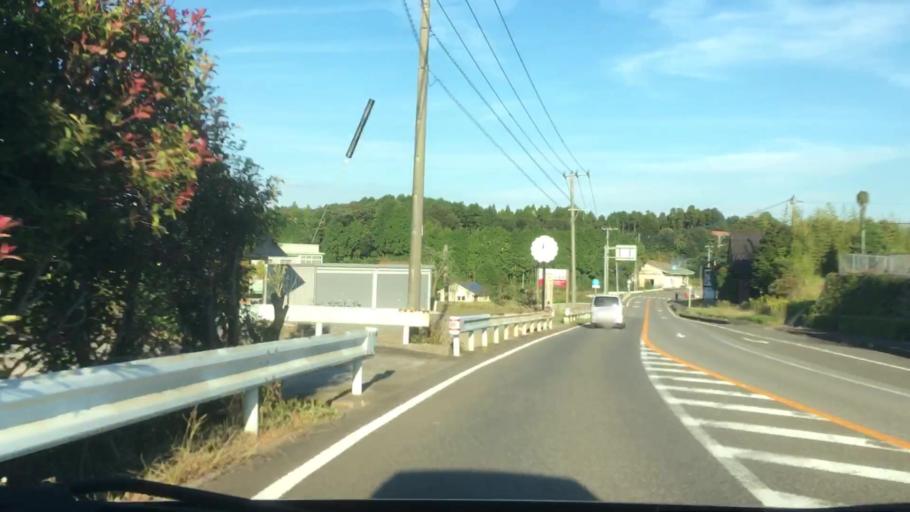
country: JP
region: Nagasaki
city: Sasebo
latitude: 33.0452
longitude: 129.6976
